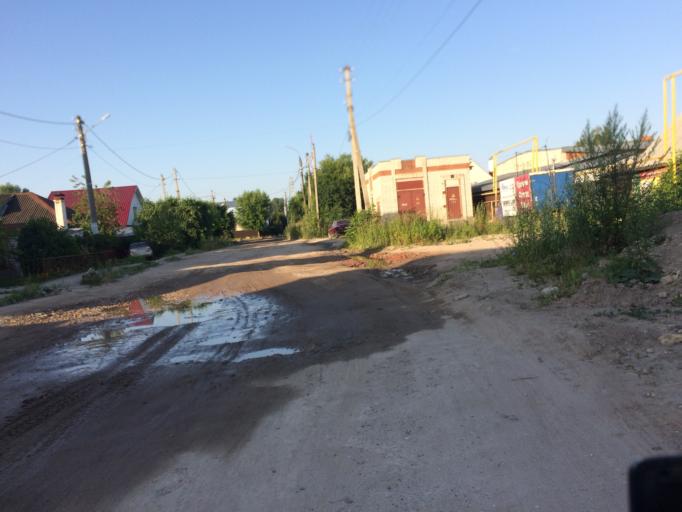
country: RU
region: Mariy-El
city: Yoshkar-Ola
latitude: 56.6553
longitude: 47.8873
